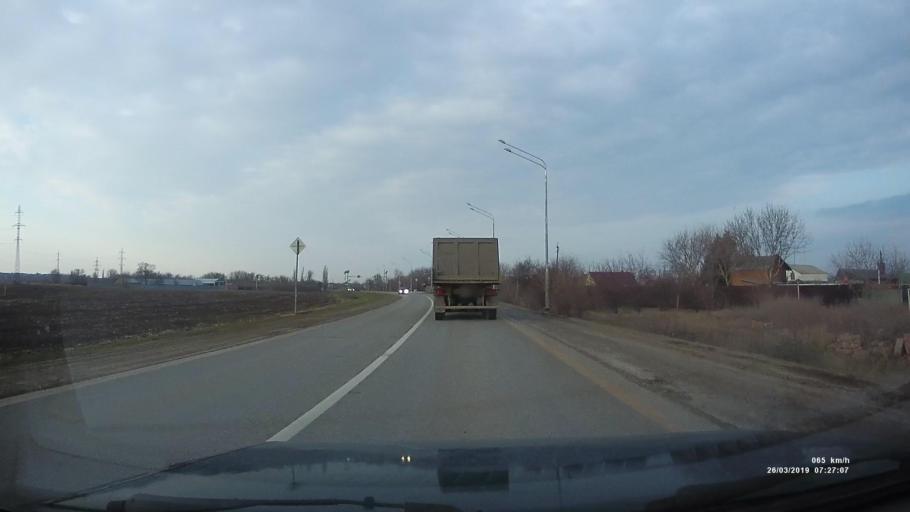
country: RU
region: Rostov
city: Taganrog
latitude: 47.2644
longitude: 38.8313
